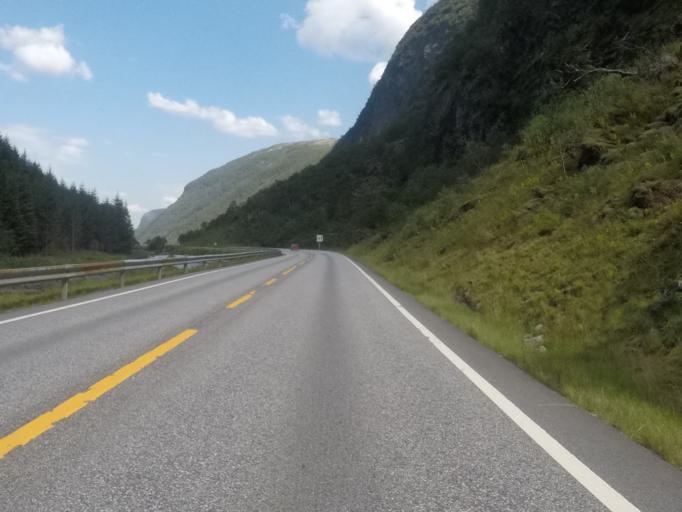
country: NO
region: Hordaland
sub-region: Masfjorden
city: Masfjorden
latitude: 60.9700
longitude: 5.4871
